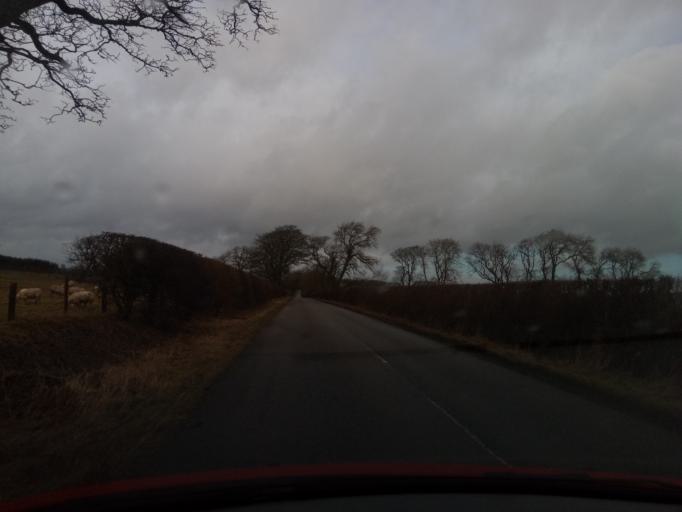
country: GB
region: England
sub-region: Northumberland
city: Rothley
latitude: 55.1804
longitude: -1.9681
